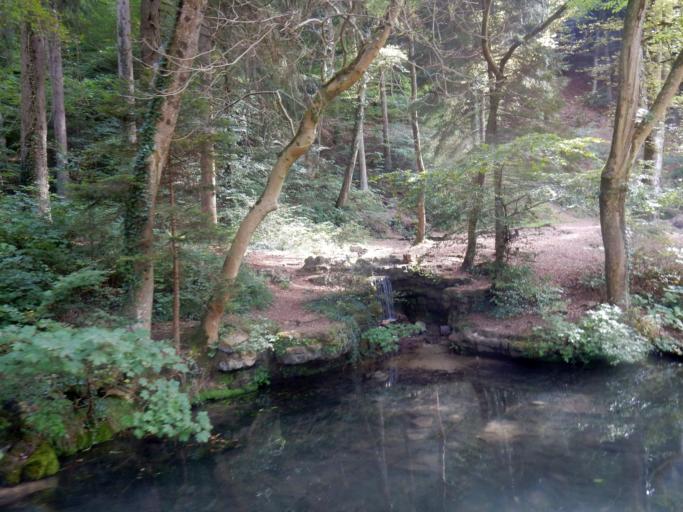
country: LU
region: Luxembourg
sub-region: Canton de Mersch
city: Mersch
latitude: 49.7266
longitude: 6.0863
